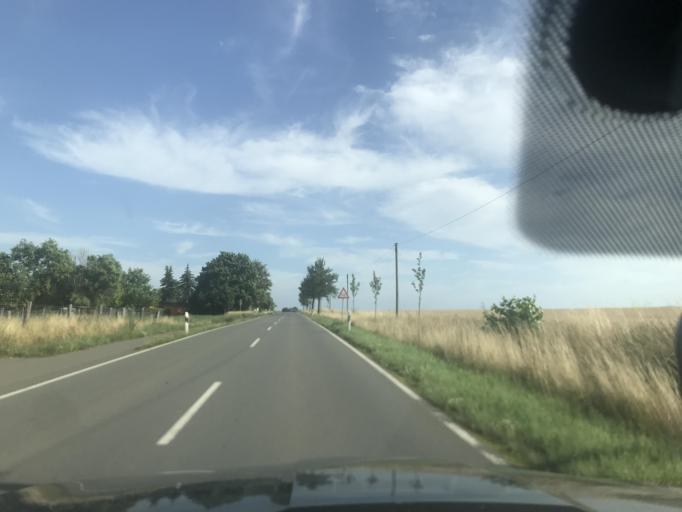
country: DE
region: Saxony-Anhalt
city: Wegeleben
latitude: 51.8764
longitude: 11.1777
